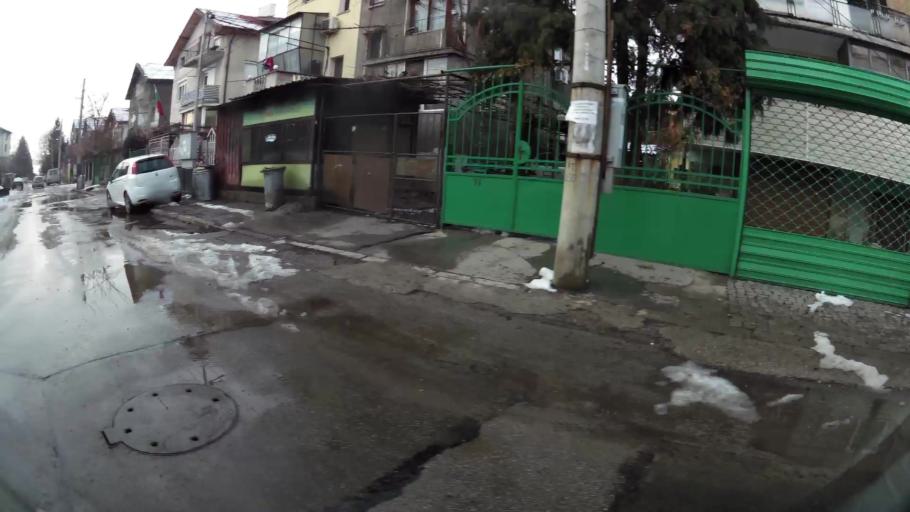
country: BG
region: Sofia-Capital
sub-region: Stolichna Obshtina
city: Sofia
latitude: 42.7250
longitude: 23.3332
